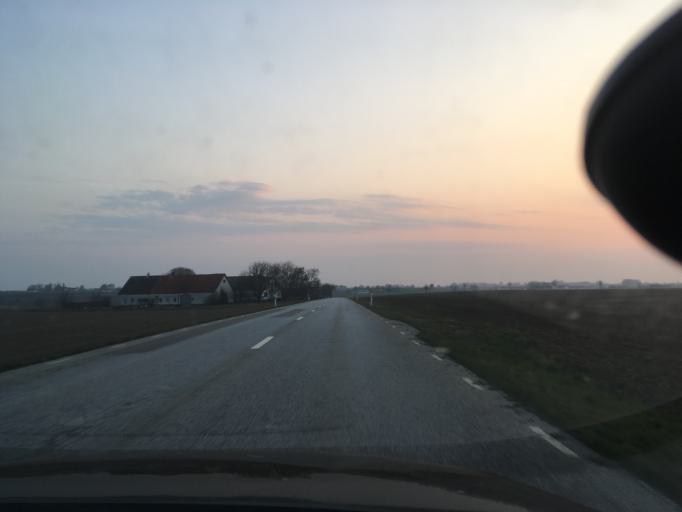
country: SE
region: Skane
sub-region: Ystads Kommun
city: Kopingebro
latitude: 55.4723
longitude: 14.0510
